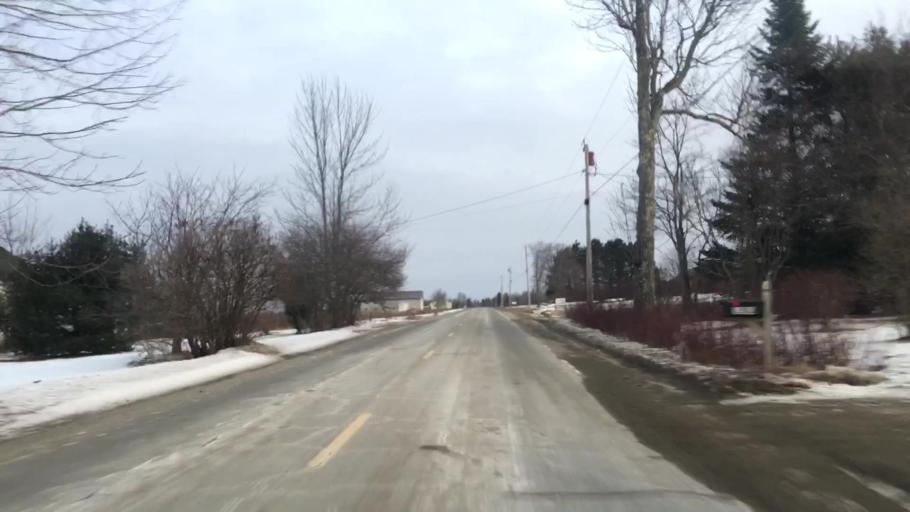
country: US
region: Maine
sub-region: Hancock County
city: Franklin
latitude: 44.7156
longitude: -68.3370
